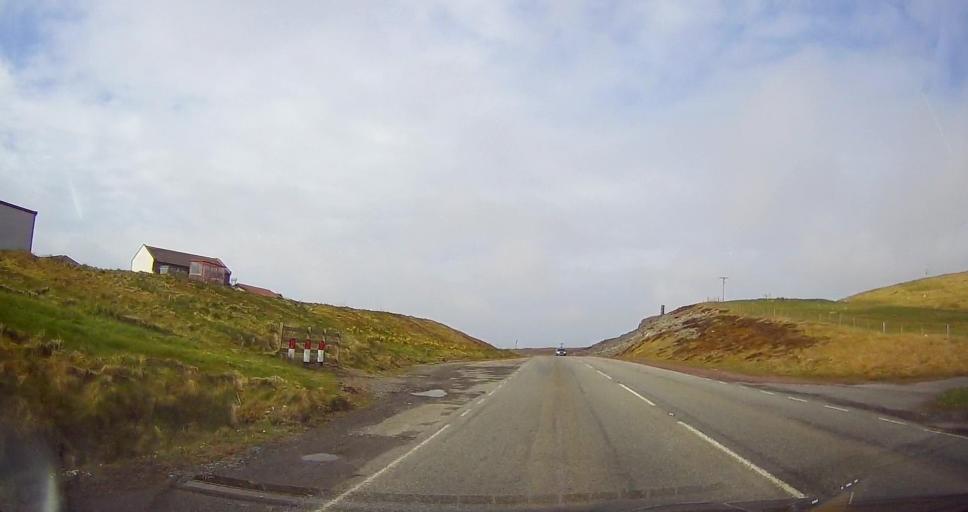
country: GB
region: Scotland
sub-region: Shetland Islands
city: Lerwick
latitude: 60.1390
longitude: -1.2003
